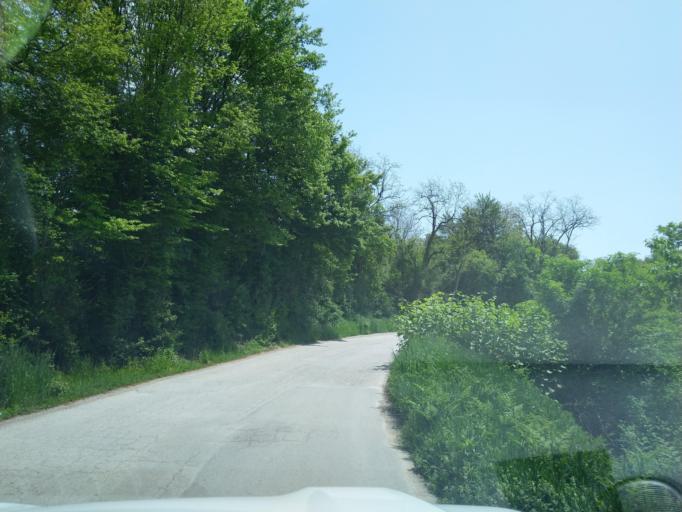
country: RS
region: Central Serbia
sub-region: Zlatiborski Okrug
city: Uzice
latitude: 43.8585
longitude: 19.9117
